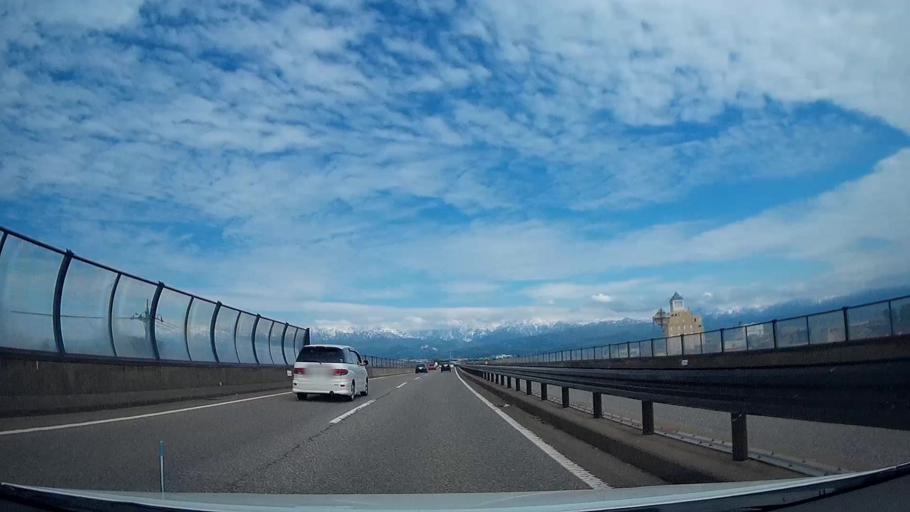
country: JP
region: Toyama
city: Toyama-shi
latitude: 36.7200
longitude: 137.2639
